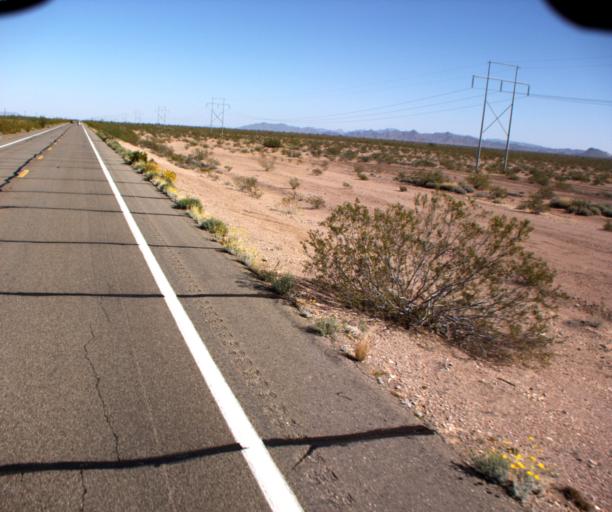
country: US
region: Arizona
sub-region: La Paz County
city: Quartzsite
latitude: 33.3568
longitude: -114.2171
